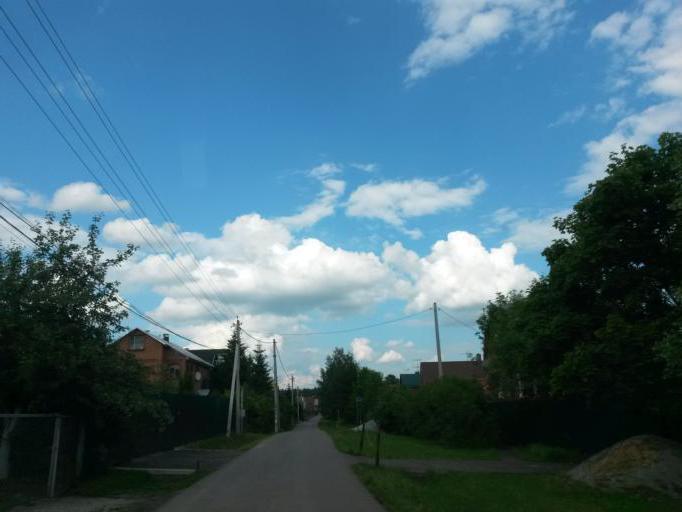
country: RU
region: Moskovskaya
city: Lyubuchany
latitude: 55.2666
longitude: 37.5600
